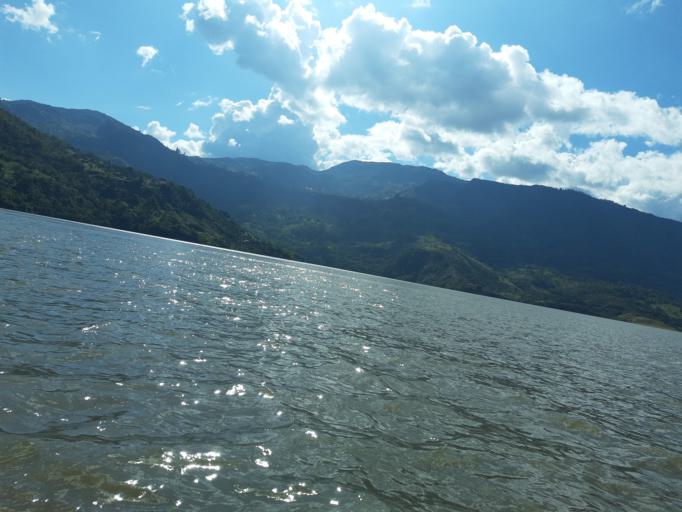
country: CO
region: Boyaca
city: Chivor
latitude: 4.9469
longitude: -73.3194
